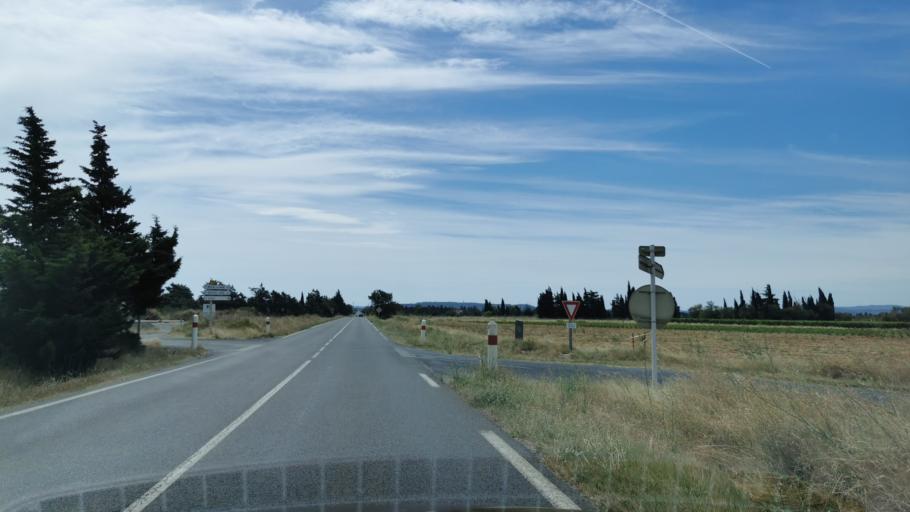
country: FR
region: Languedoc-Roussillon
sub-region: Departement de l'Aude
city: Ginestas
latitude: 43.2699
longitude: 2.8942
